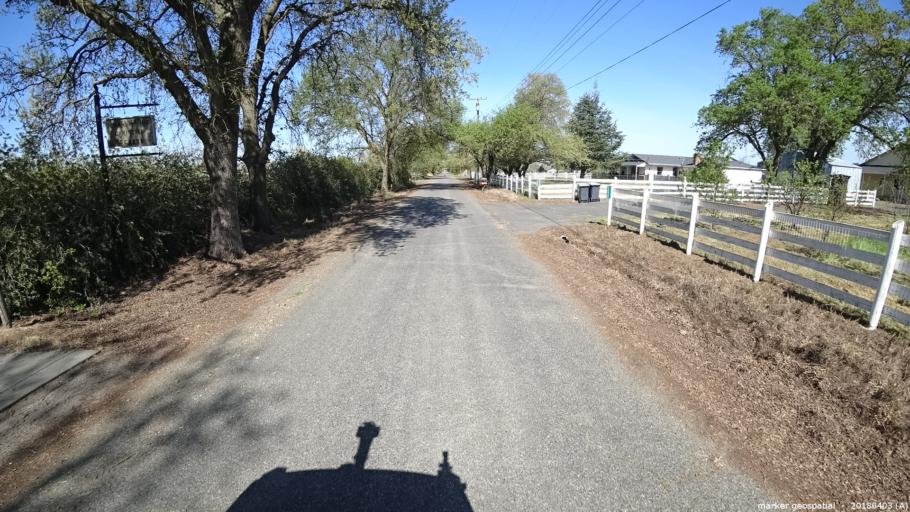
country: US
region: California
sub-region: Sacramento County
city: Wilton
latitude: 38.4303
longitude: -121.2078
